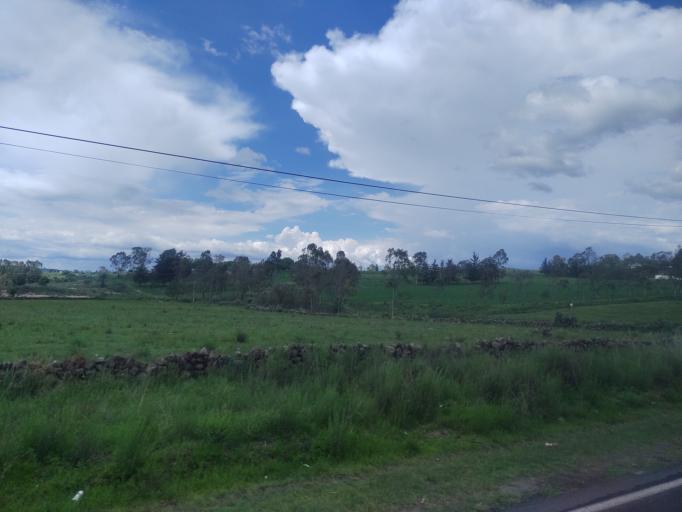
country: MX
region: Mexico
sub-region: Aculco
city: El Colorado
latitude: 20.0916
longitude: -99.7790
